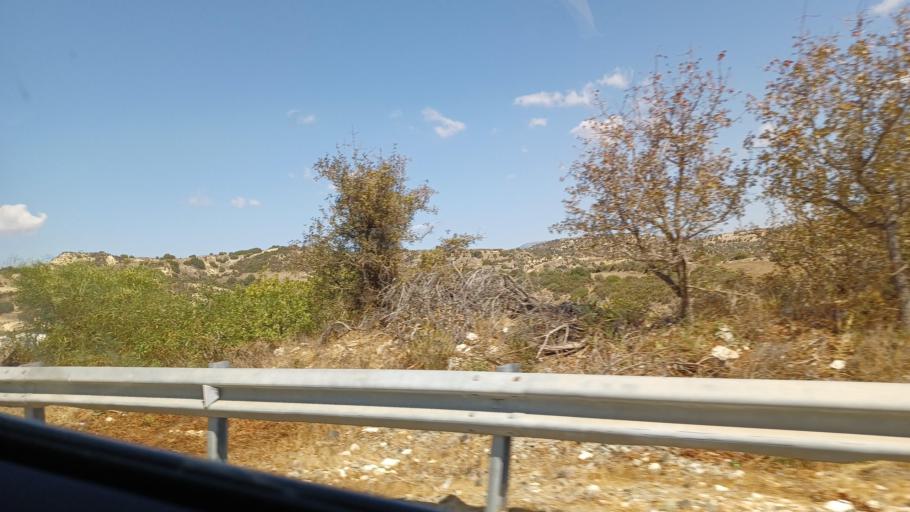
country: CY
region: Pafos
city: Mesogi
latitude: 34.7910
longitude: 32.5483
